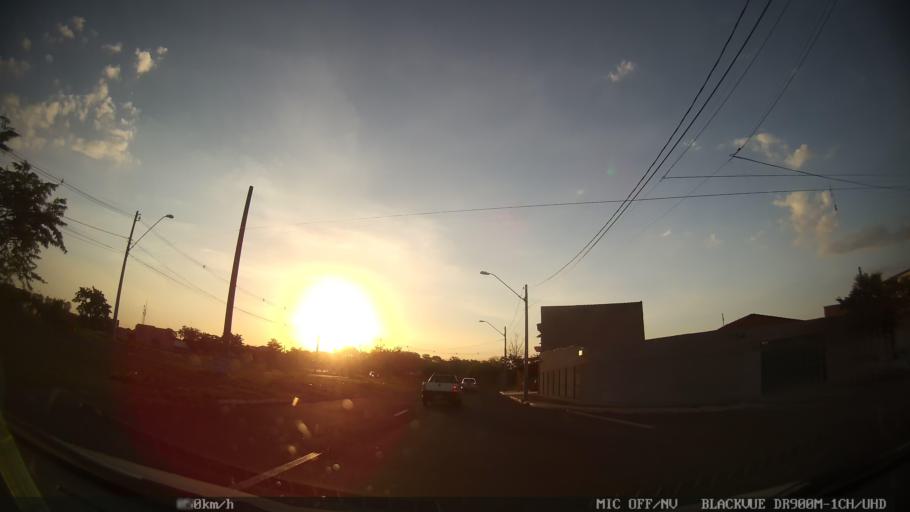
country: BR
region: Sao Paulo
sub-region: Ribeirao Preto
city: Ribeirao Preto
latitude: -21.1474
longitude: -47.8509
